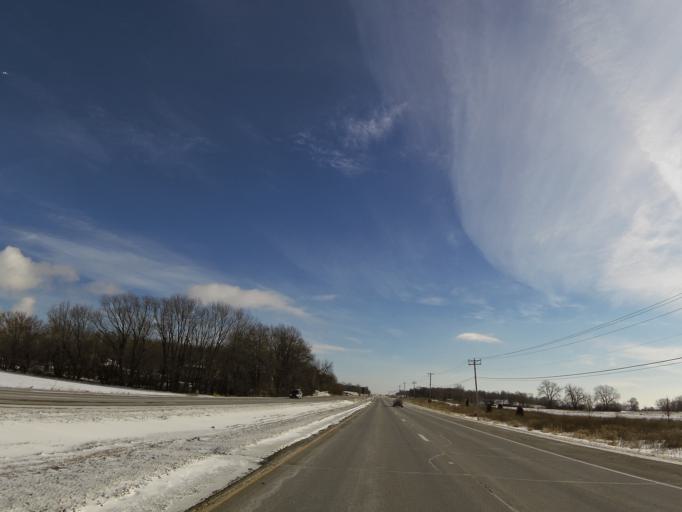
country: US
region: Minnesota
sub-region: Dakota County
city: Rosemount
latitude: 44.7389
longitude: -93.0687
